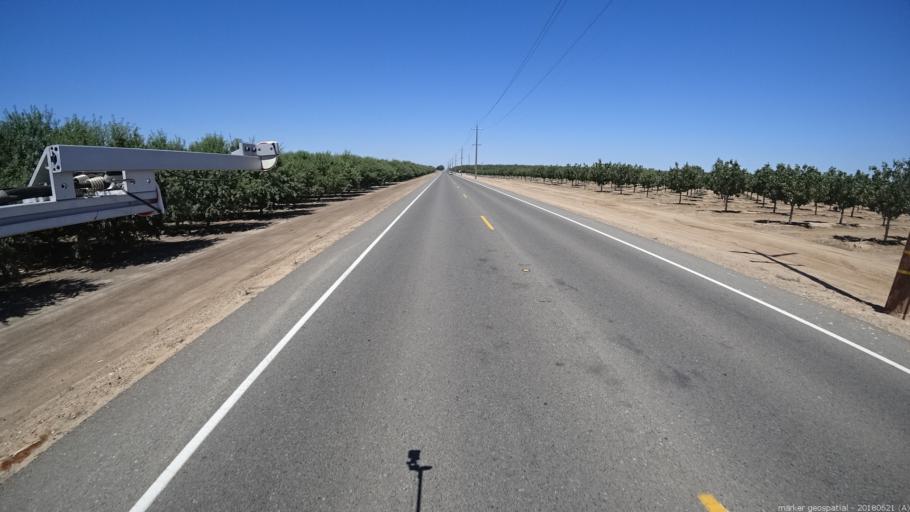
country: US
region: California
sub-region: Madera County
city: Bonadelle Ranchos-Madera Ranchos
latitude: 36.8803
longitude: -119.9027
